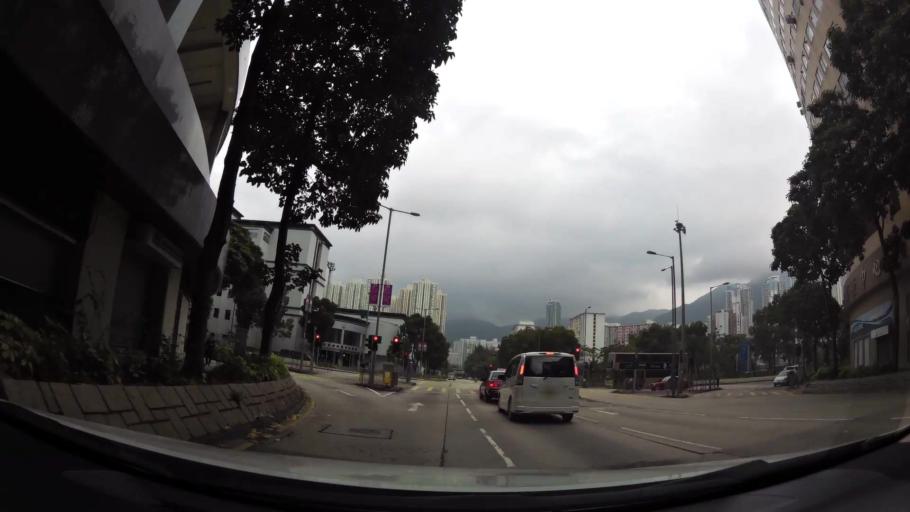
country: HK
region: Kowloon City
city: Kowloon
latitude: 22.3250
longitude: 114.2087
